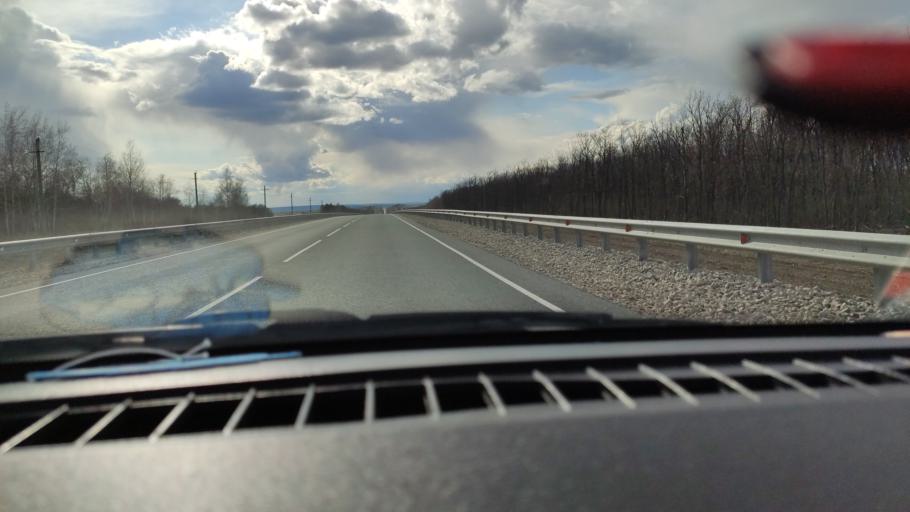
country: RU
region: Saratov
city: Shikhany
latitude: 52.1611
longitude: 47.1529
